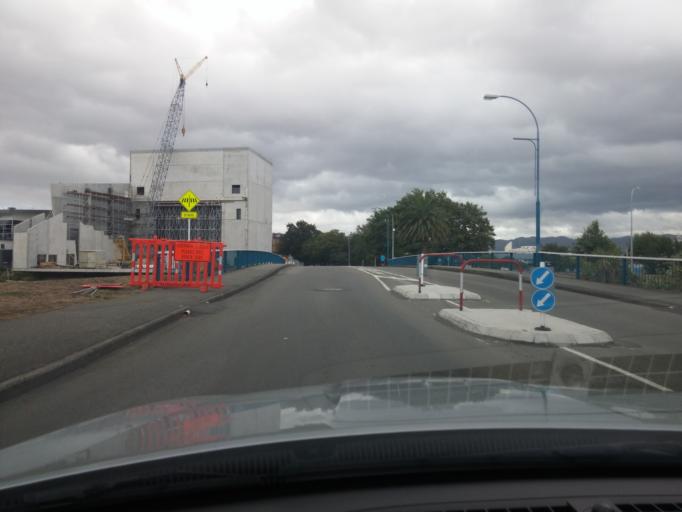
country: NZ
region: Marlborough
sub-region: Marlborough District
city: Blenheim
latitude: -41.5091
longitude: 173.9559
